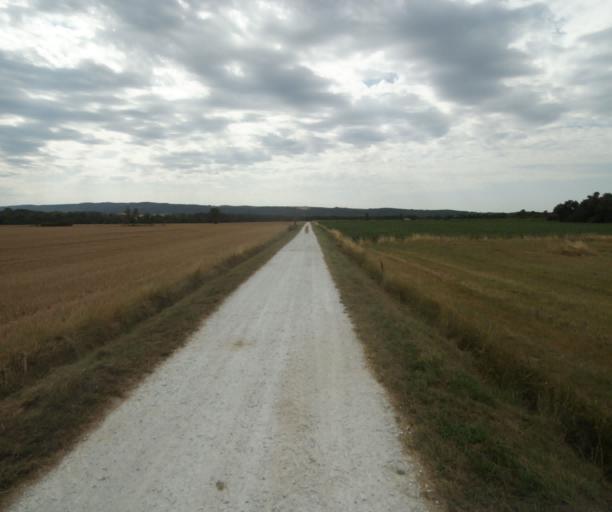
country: FR
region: Midi-Pyrenees
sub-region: Departement de la Haute-Garonne
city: Saint-Felix-Lauragais
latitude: 43.4378
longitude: 1.9424
